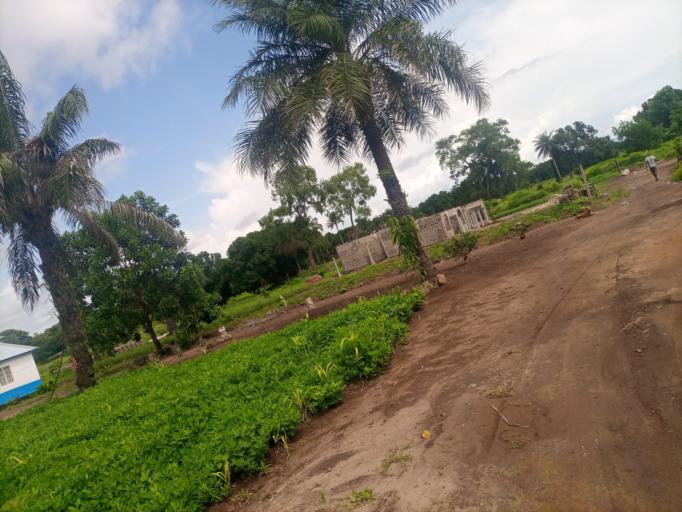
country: SL
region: Northern Province
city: Sawkta
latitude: 8.6366
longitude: -13.2081
